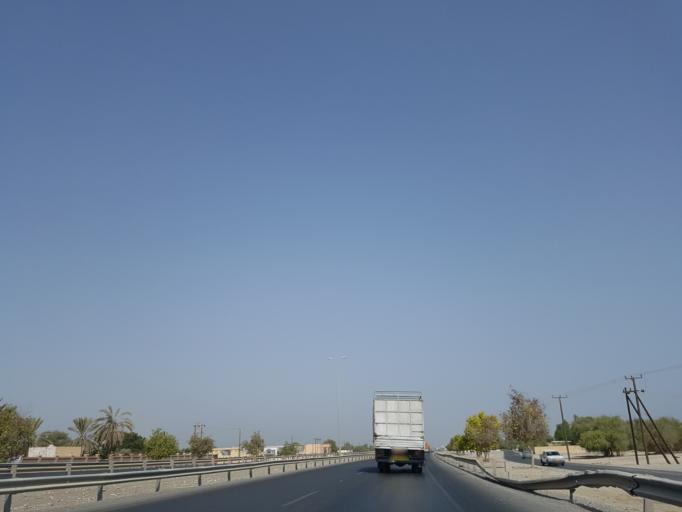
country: OM
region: Al Batinah
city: As Suwayq
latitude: 23.7551
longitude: 57.5634
